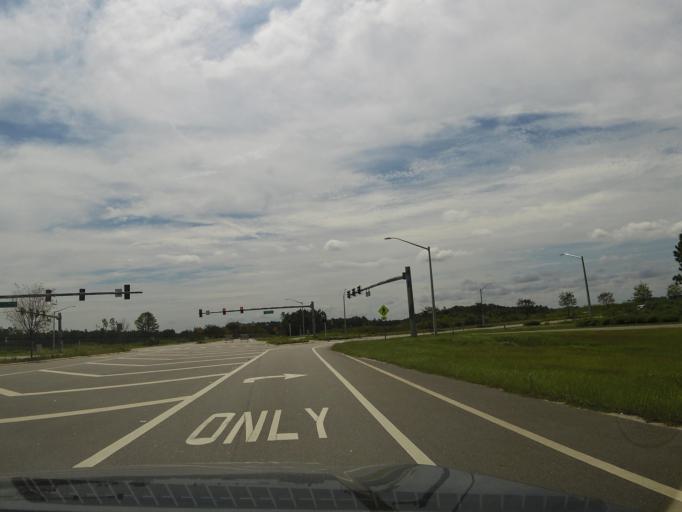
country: US
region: Florida
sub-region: Clay County
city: Green Cove Springs
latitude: 30.0028
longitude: -81.5040
